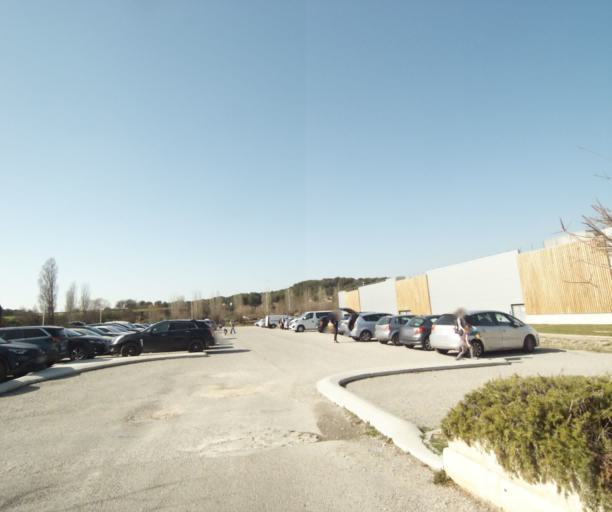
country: FR
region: Provence-Alpes-Cote d'Azur
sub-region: Departement des Bouches-du-Rhone
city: Cabries
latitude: 43.4305
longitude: 5.3988
